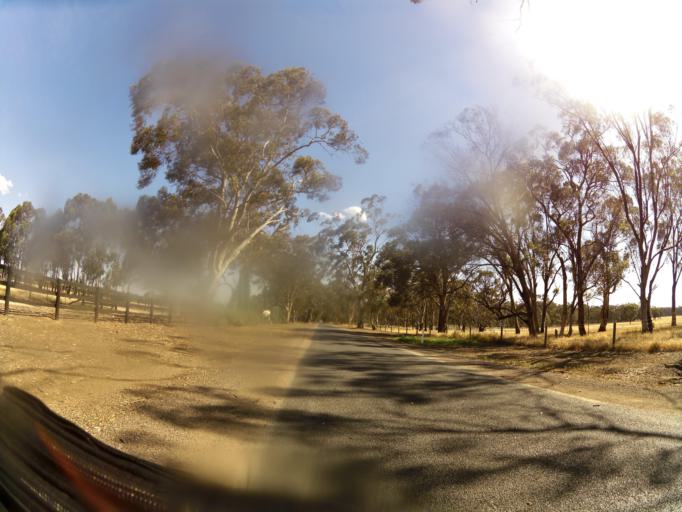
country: AU
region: Victoria
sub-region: Campaspe
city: Kyabram
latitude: -36.8653
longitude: 145.0874
